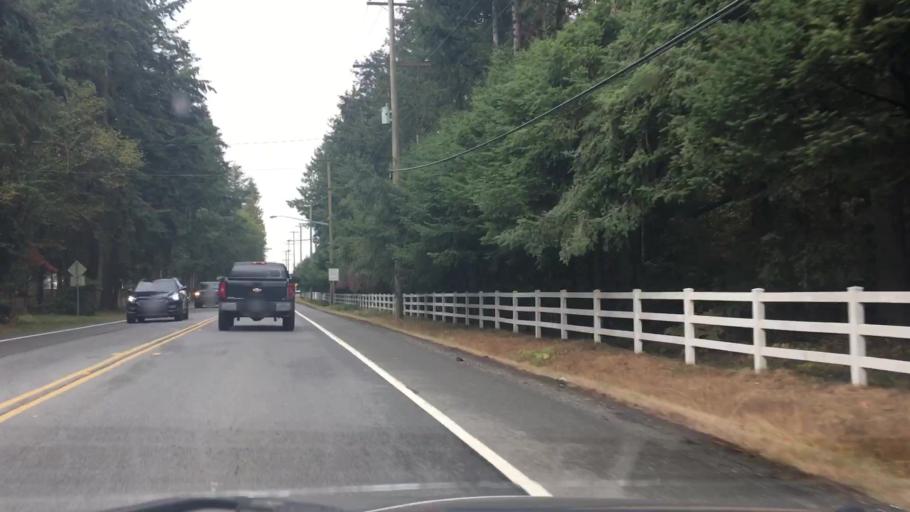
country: CA
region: British Columbia
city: Langley
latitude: 49.1041
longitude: -122.5606
